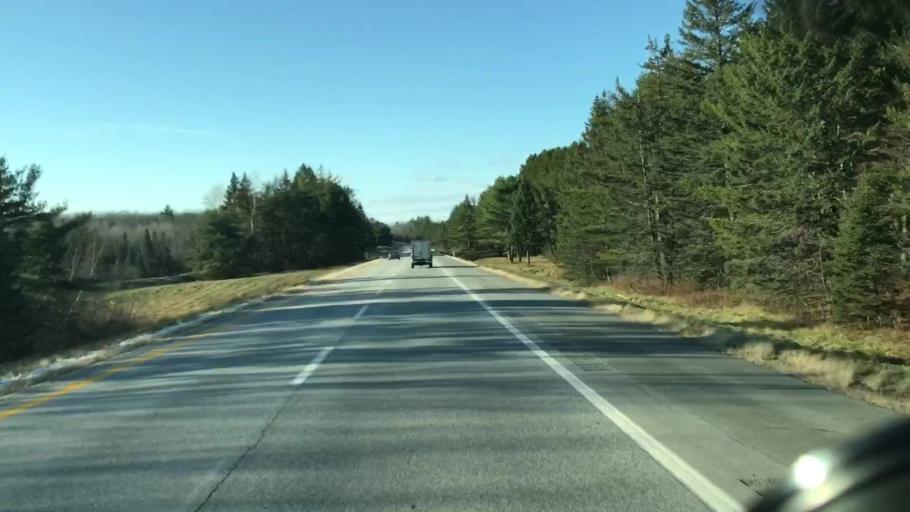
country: US
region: Maine
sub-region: Penobscot County
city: Carmel
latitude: 44.7687
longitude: -68.9975
